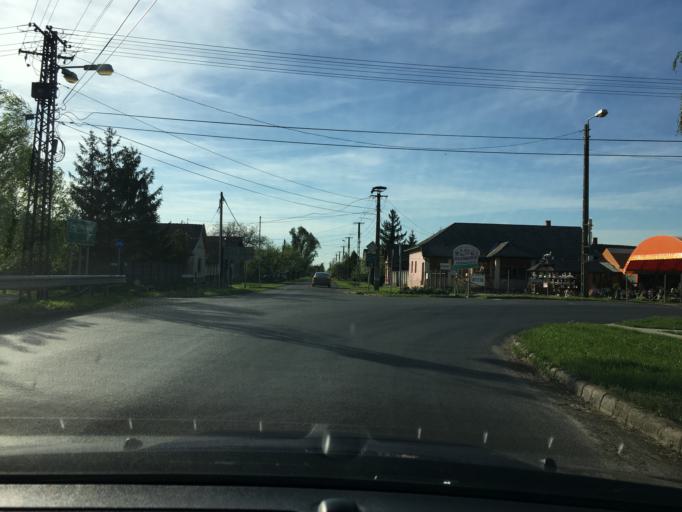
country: HU
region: Bekes
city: Korostarcsa
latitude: 46.8743
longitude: 21.0199
